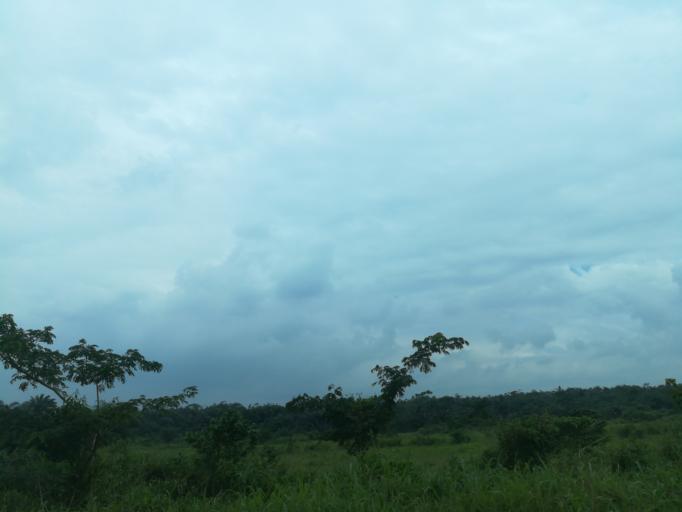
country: NG
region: Lagos
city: Ejirin
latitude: 6.6567
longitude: 3.8027
